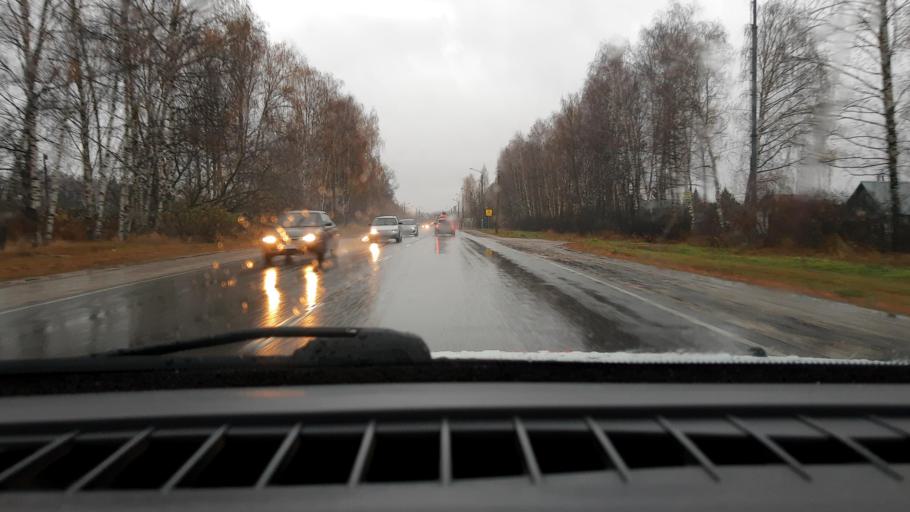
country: RU
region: Nizjnij Novgorod
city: Sitniki
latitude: 56.4607
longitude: 44.0306
